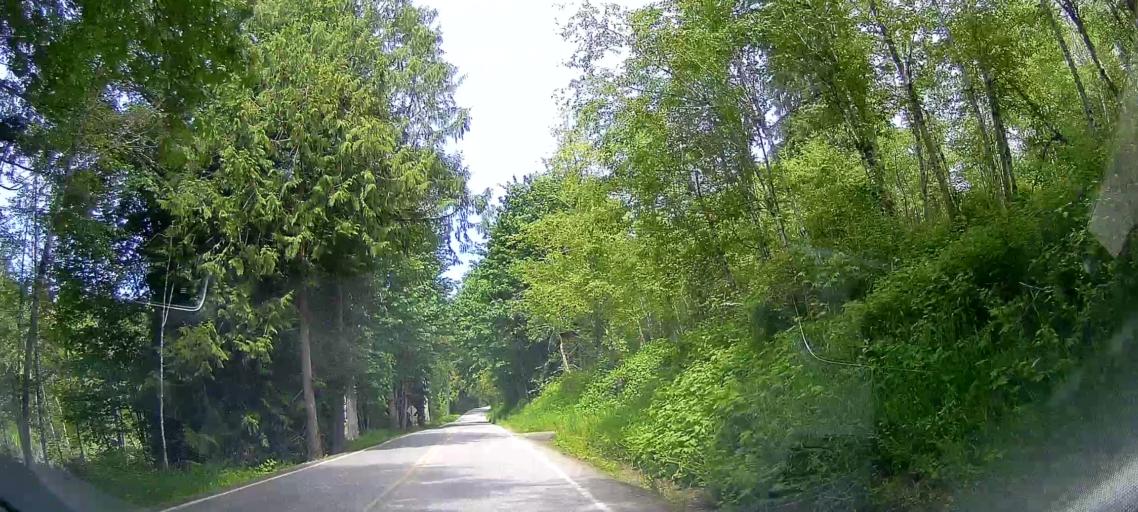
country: US
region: Washington
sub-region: Snohomish County
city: Bryant
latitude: 48.3202
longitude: -122.1587
